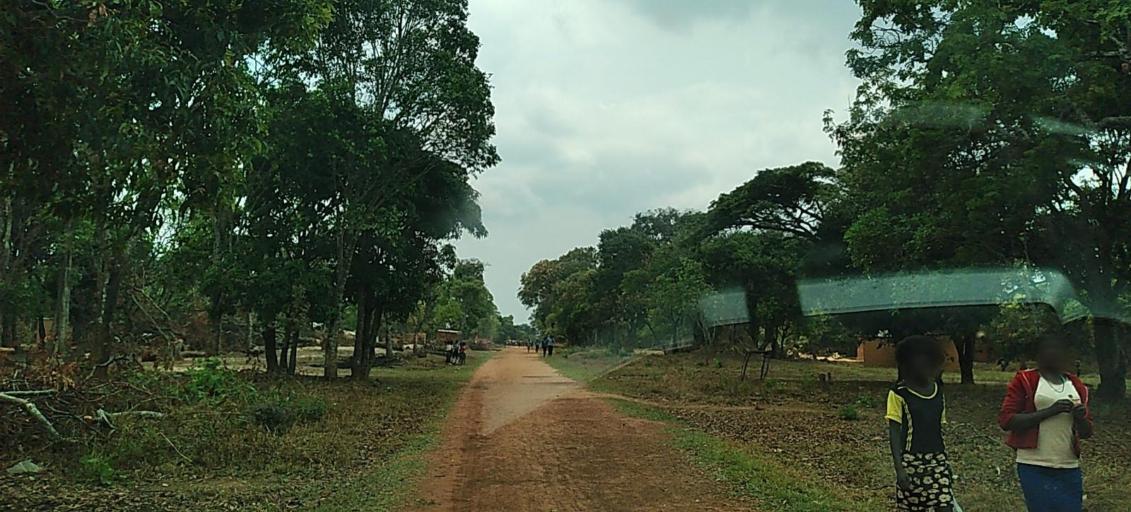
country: ZM
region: North-Western
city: Mwinilunga
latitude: -11.5265
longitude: 24.7864
